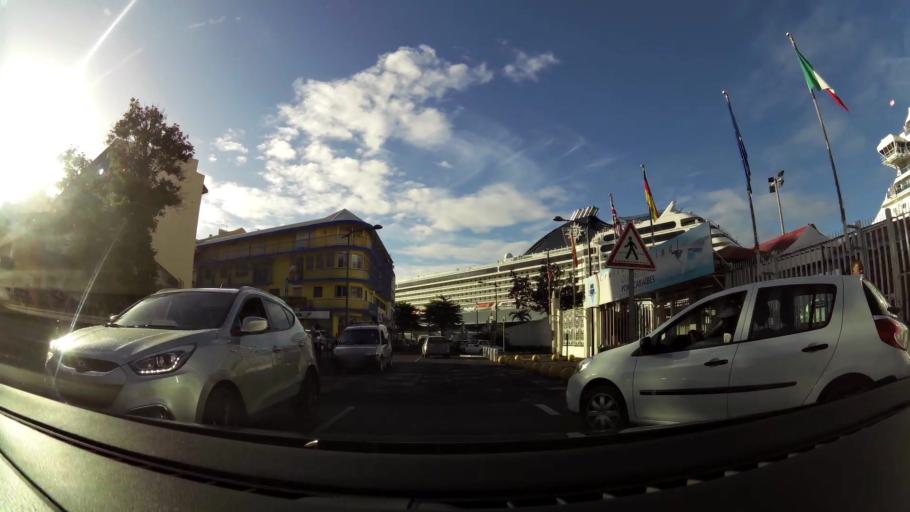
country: GP
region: Guadeloupe
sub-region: Guadeloupe
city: Pointe-a-Pitre
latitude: 16.2377
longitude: -61.5389
